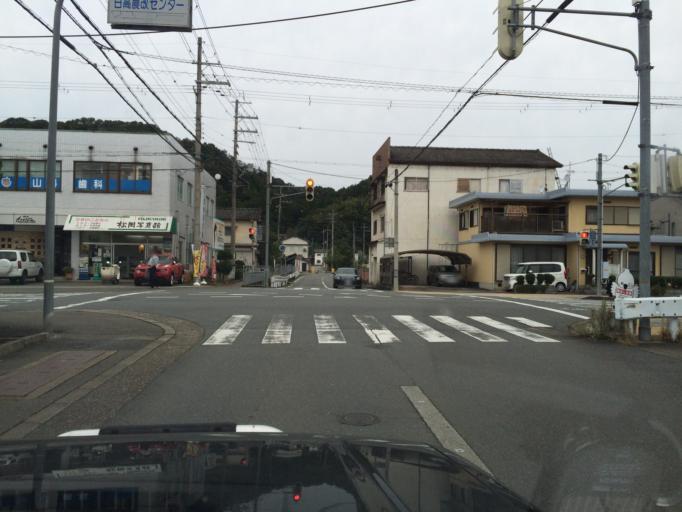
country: JP
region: Hyogo
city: Toyooka
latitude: 35.4699
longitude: 134.7740
